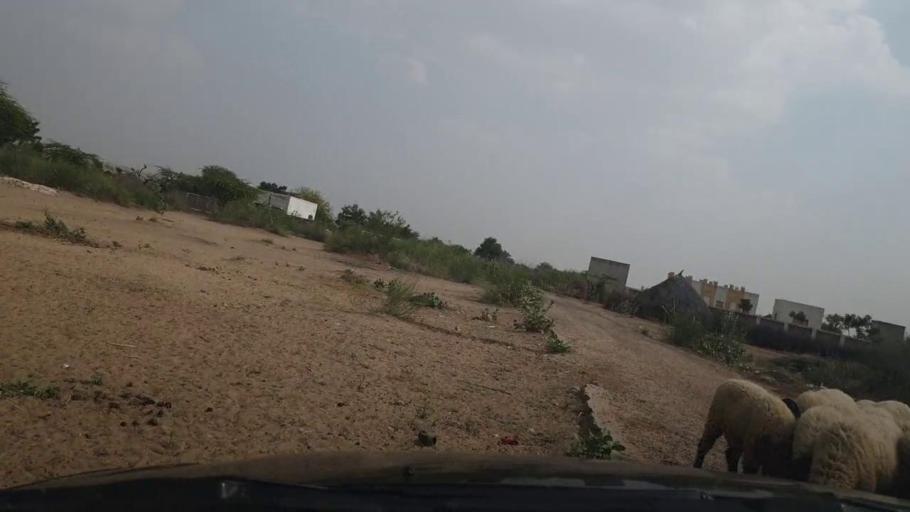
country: PK
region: Sindh
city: Islamkot
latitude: 24.9353
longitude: 70.5662
